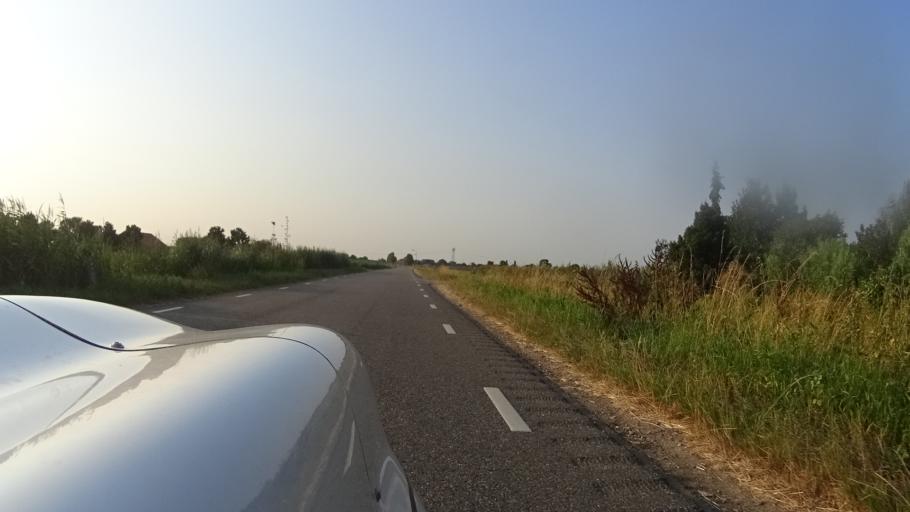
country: NL
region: Gelderland
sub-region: Gemeente Buren
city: Lienden
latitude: 51.8635
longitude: 5.5153
